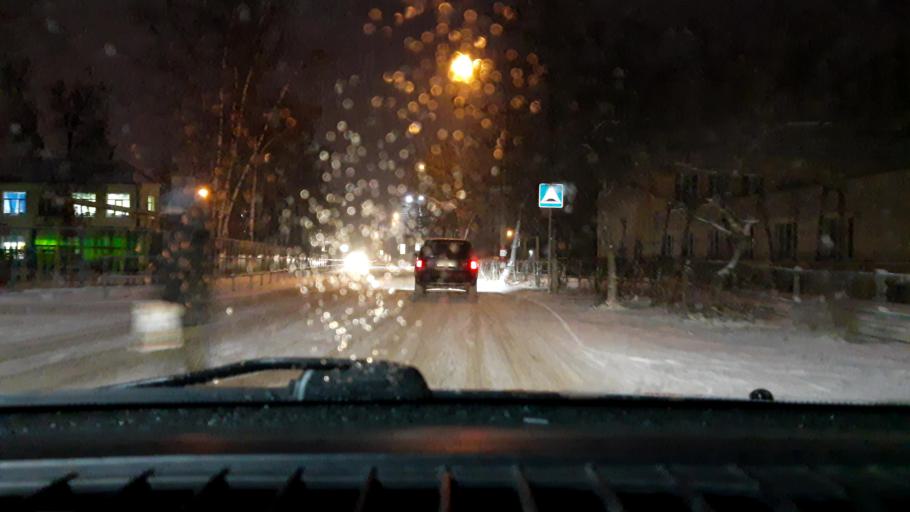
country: RU
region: Nizjnij Novgorod
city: Bor
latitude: 56.3340
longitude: 44.1136
